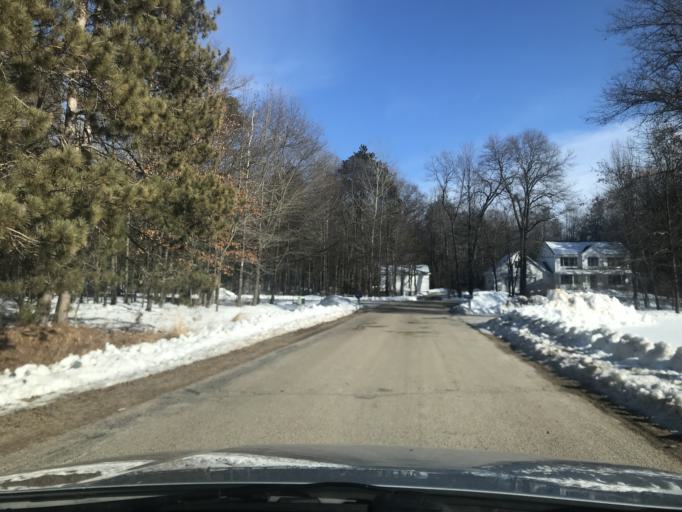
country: US
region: Wisconsin
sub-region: Marinette County
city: Peshtigo
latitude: 45.0294
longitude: -87.7057
